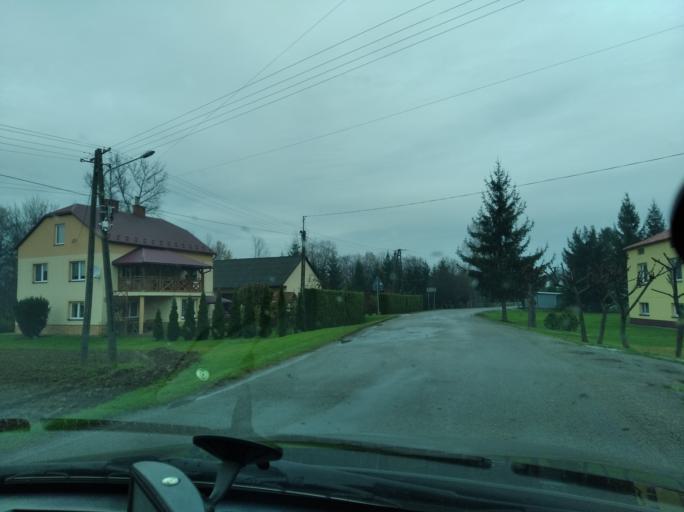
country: PL
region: Subcarpathian Voivodeship
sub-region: Powiat strzyzowski
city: Babica
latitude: 49.9274
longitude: 21.8719
